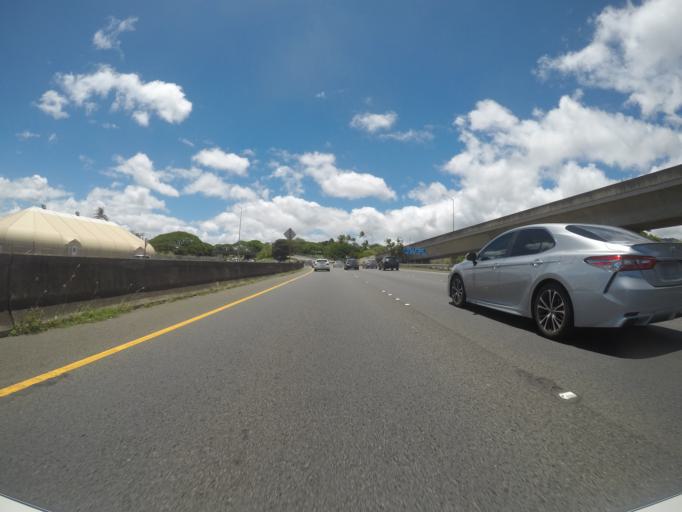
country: US
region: Hawaii
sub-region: Honolulu County
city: Honolulu
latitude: 21.3409
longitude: -157.8858
